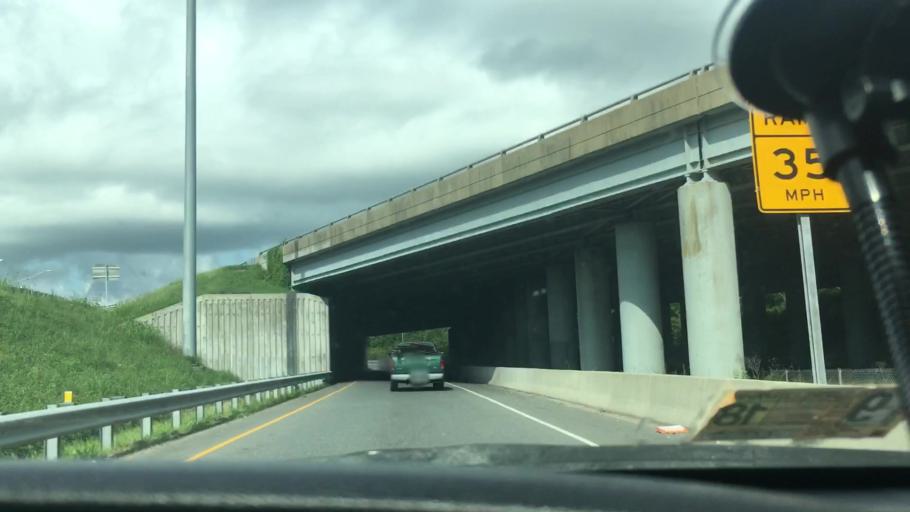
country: US
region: Virginia
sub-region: City of Virginia Beach
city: Virginia Beach
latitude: 36.8387
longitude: -76.0539
